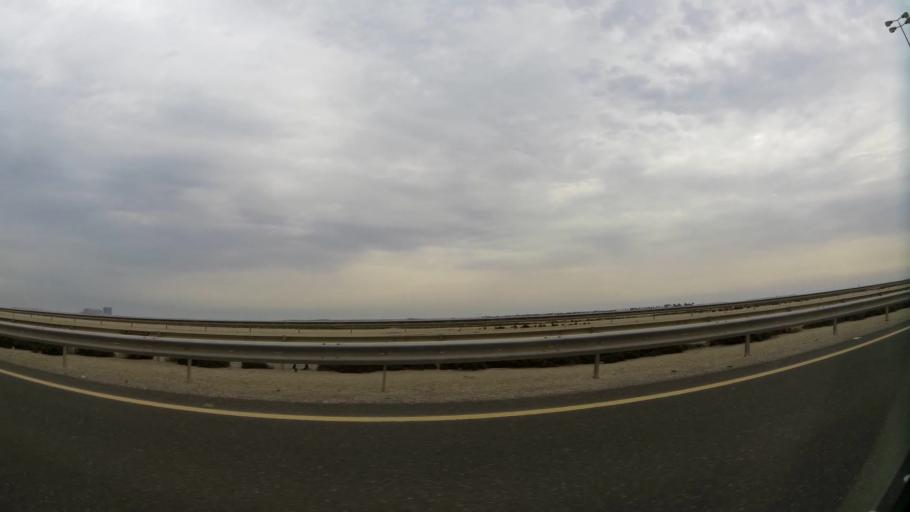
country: BH
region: Central Governorate
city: Dar Kulayb
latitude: 25.8545
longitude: 50.5846
